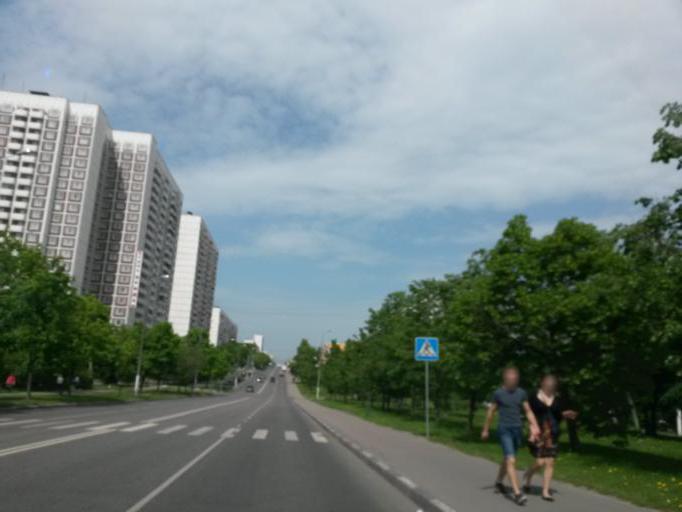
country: RU
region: Moscow
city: Chertanovo Yuzhnoye
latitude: 55.6052
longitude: 37.6007
